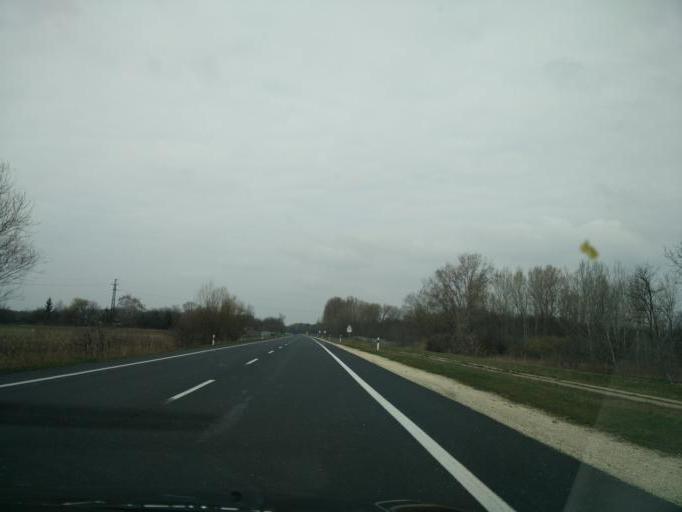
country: HU
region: Gyor-Moson-Sopron
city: Toltestava
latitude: 47.7068
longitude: 17.7558
